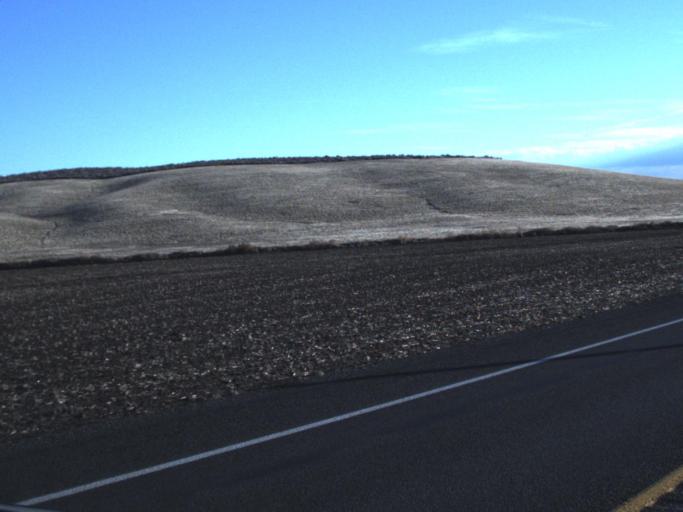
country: US
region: Washington
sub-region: Garfield County
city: Pomeroy
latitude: 46.7371
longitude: -117.7403
